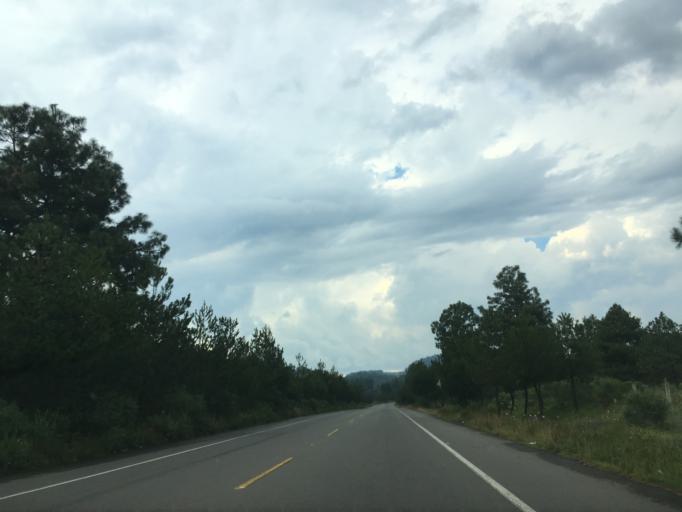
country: MX
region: Michoacan
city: Angahuan
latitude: 19.5383
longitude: -102.2000
